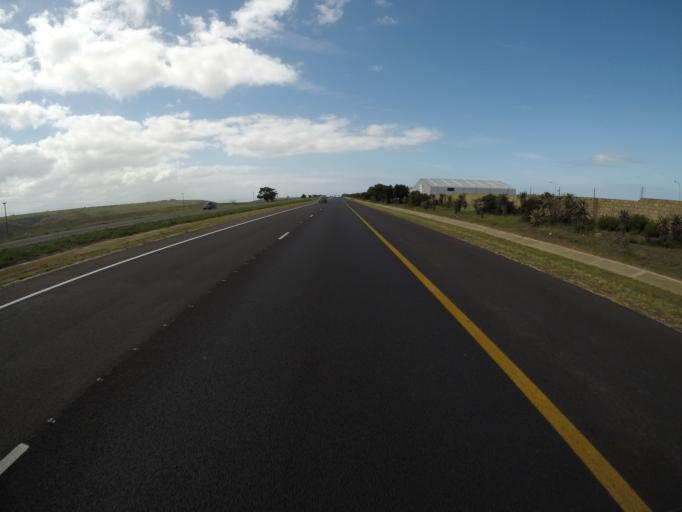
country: ZA
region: Western Cape
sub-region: Eden District Municipality
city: Mossel Bay
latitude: -34.1709
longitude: 22.0745
